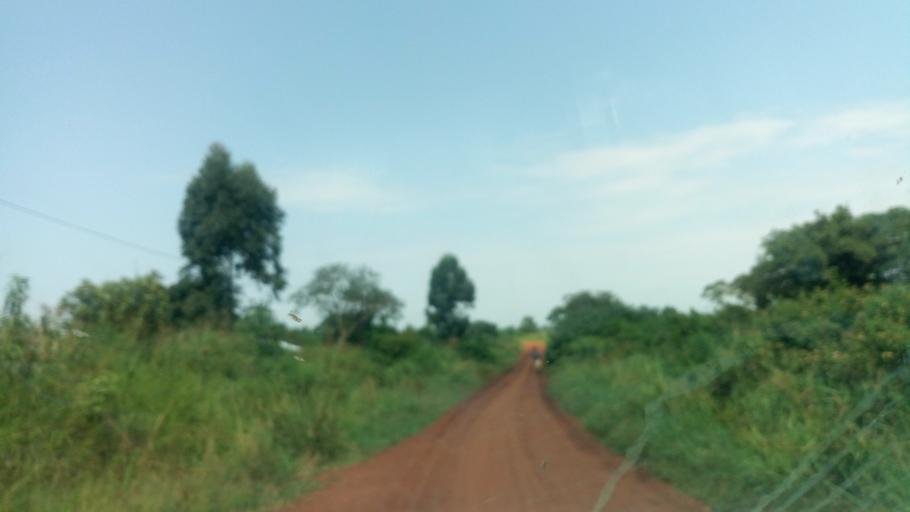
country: UG
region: Western Region
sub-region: Masindi District
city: Masindi
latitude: 1.6843
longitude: 31.8345
